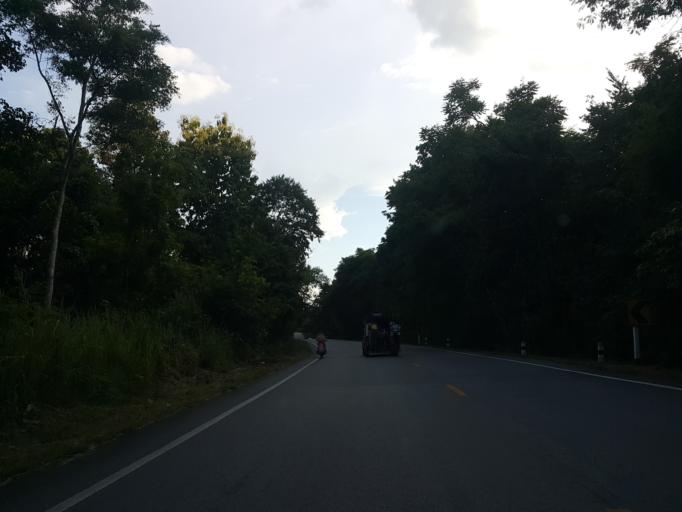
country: TH
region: Chiang Mai
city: Mae Taeng
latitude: 19.0811
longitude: 98.9796
